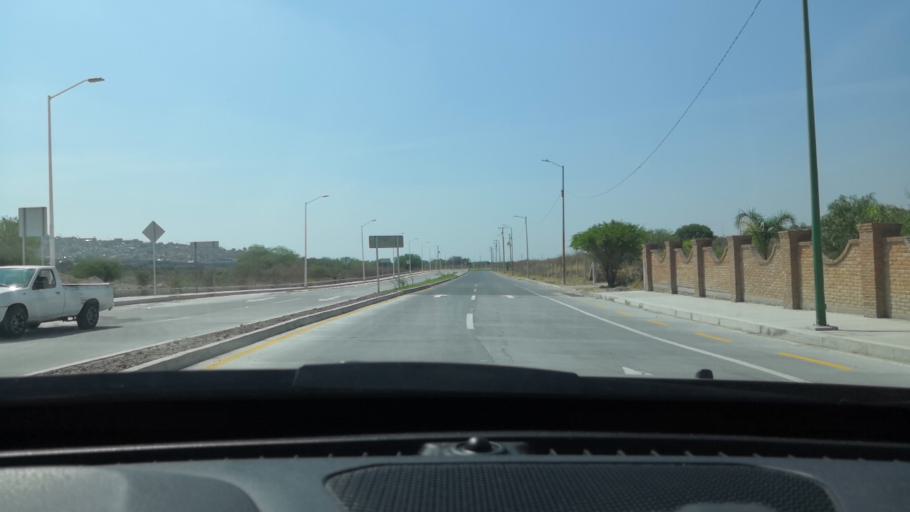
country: MX
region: Guanajuato
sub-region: Purisima del Rincon
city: Potrerillos (Guanajal)
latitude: 21.0582
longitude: -101.8680
